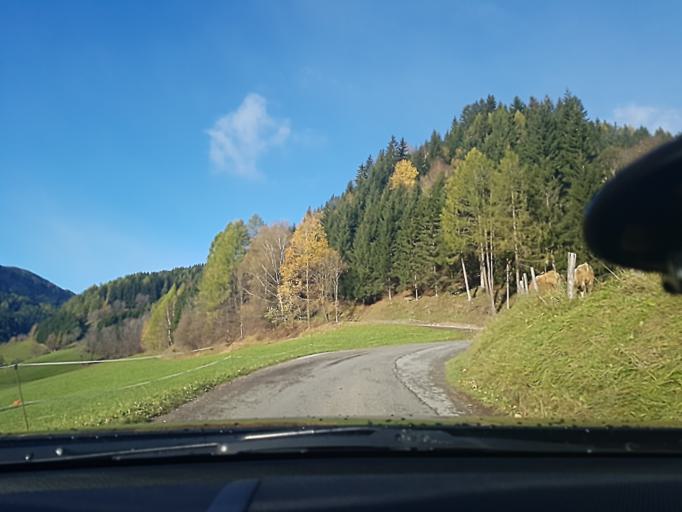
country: AT
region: Styria
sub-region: Politischer Bezirk Murtal
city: Oberzeiring
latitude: 47.2534
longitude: 14.4613
